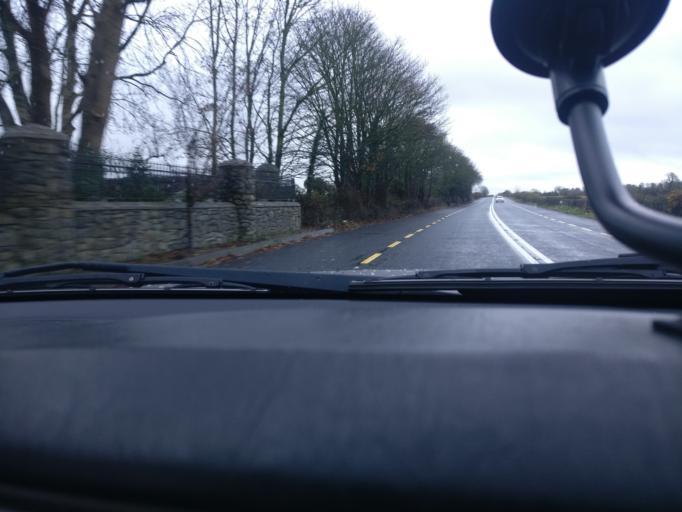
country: IE
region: Leinster
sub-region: An Mhi
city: Longwood
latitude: 53.4256
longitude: -6.8841
